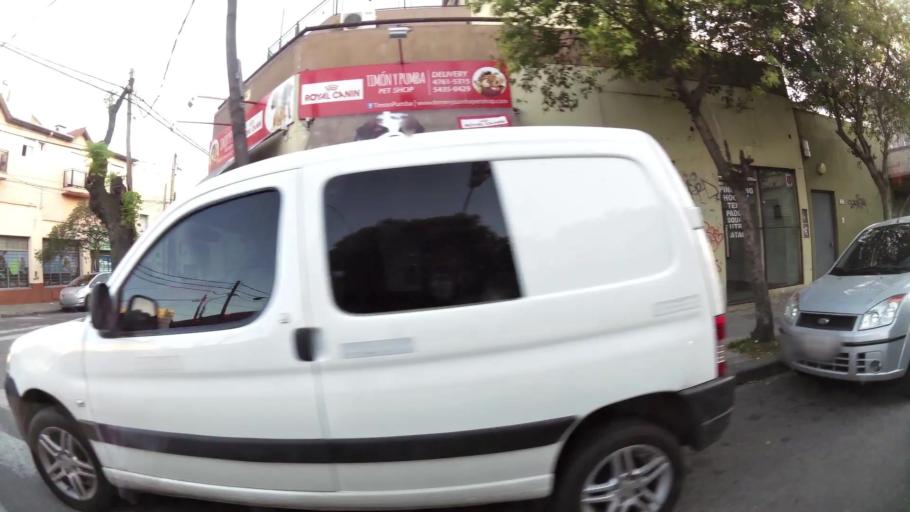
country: AR
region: Buenos Aires
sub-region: Partido de Vicente Lopez
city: Olivos
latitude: -34.5351
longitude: -58.5067
